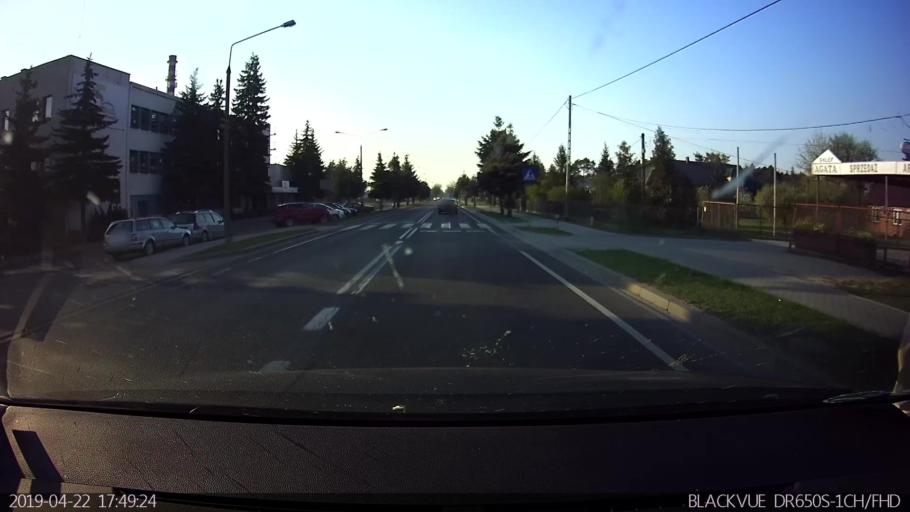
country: PL
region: Masovian Voivodeship
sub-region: Powiat wegrowski
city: Wegrow
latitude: 52.4137
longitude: 22.0090
